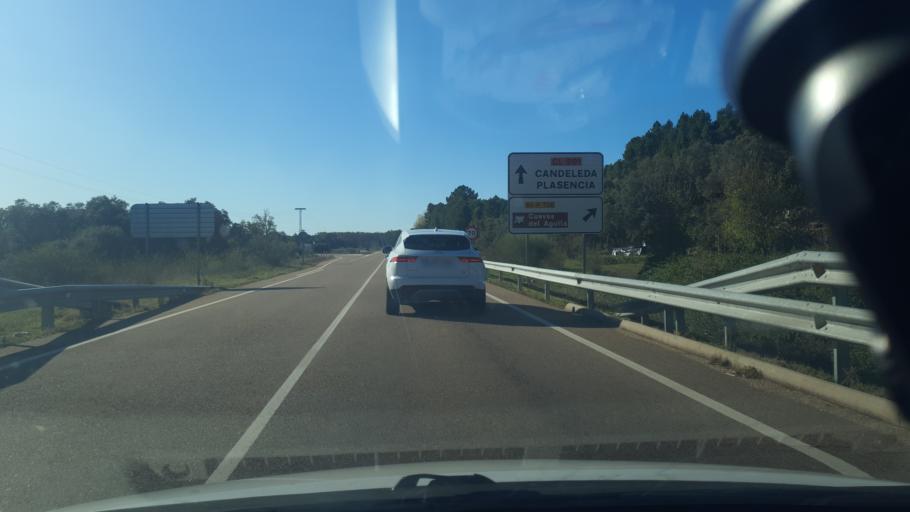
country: ES
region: Castille and Leon
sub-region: Provincia de Avila
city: Arenas de San Pedro
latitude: 40.1812
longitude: -5.0865
